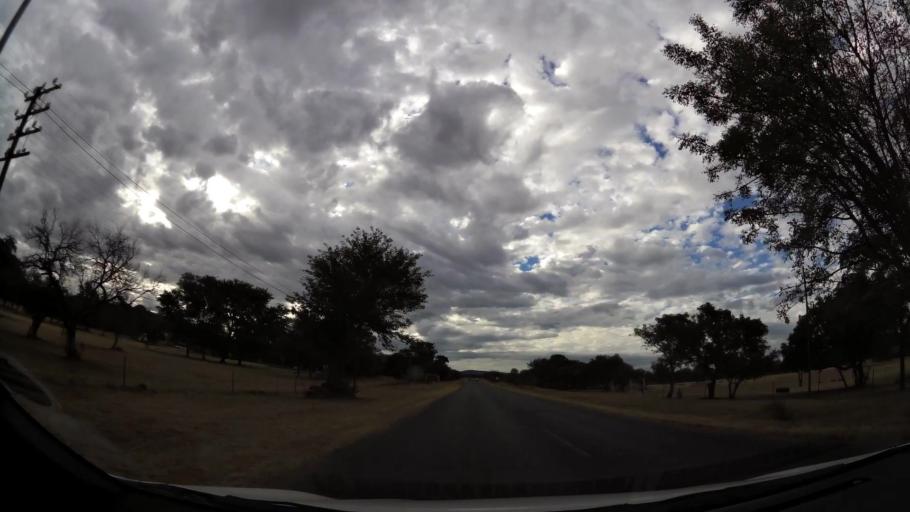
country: ZA
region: Limpopo
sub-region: Waterberg District Municipality
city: Modimolle
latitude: -24.5110
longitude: 28.7055
